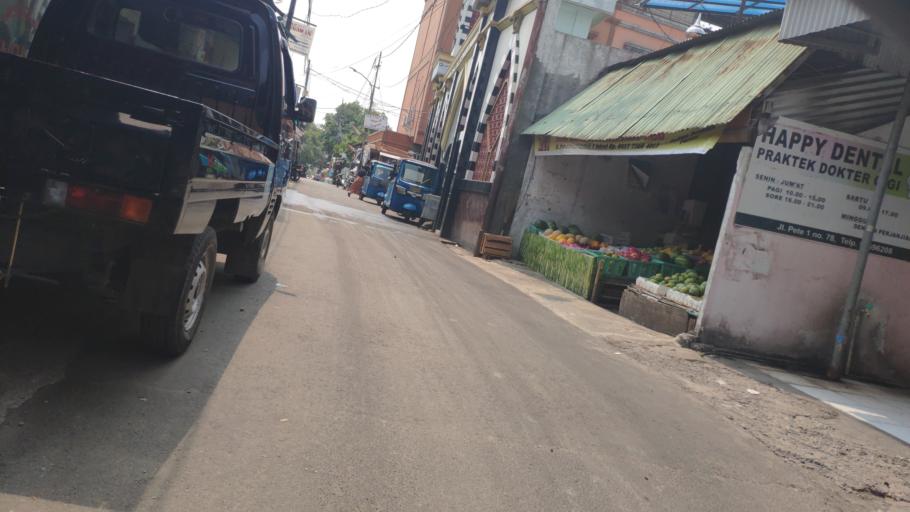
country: ID
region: Jakarta Raya
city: Jakarta
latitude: -6.2564
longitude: 106.7965
